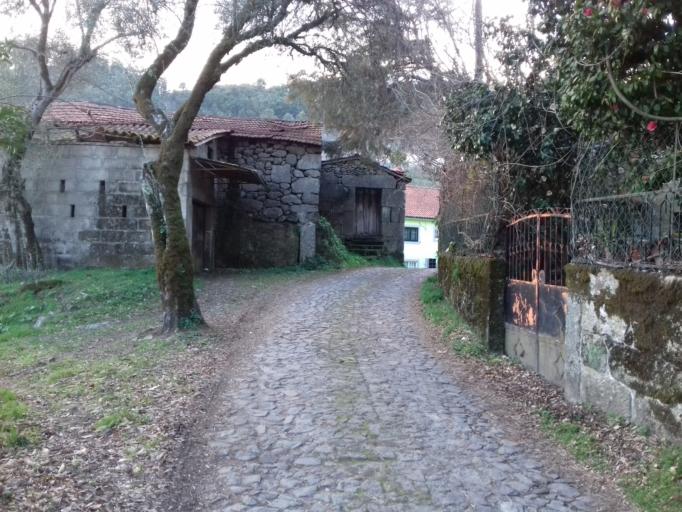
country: PT
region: Braga
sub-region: Cabeceiras de Basto
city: Refojos de Basto
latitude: 41.5281
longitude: -8.0205
